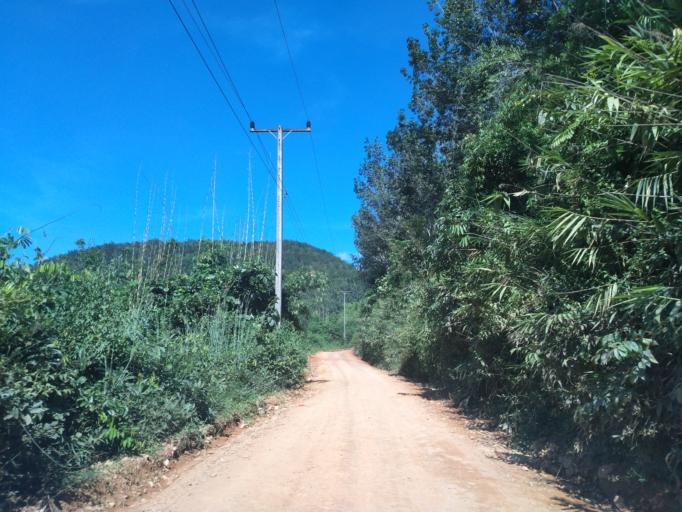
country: TH
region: Changwat Bueng Kan
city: Pak Khat
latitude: 18.6300
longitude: 103.0710
